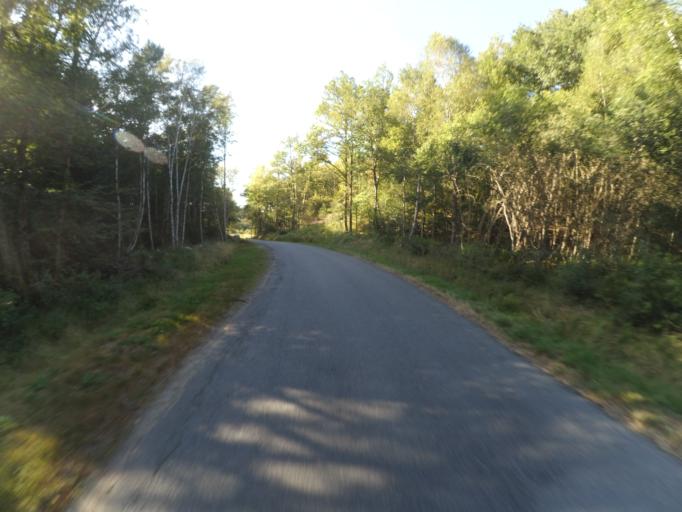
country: FR
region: Limousin
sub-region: Departement de la Creuse
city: Banize
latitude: 45.7888
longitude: 1.9699
